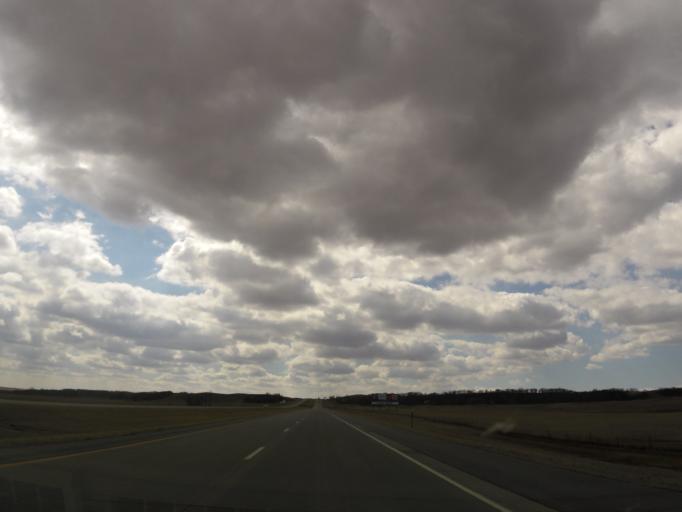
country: US
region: South Dakota
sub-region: Roberts County
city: Sisseton
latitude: 45.4329
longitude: -96.9973
